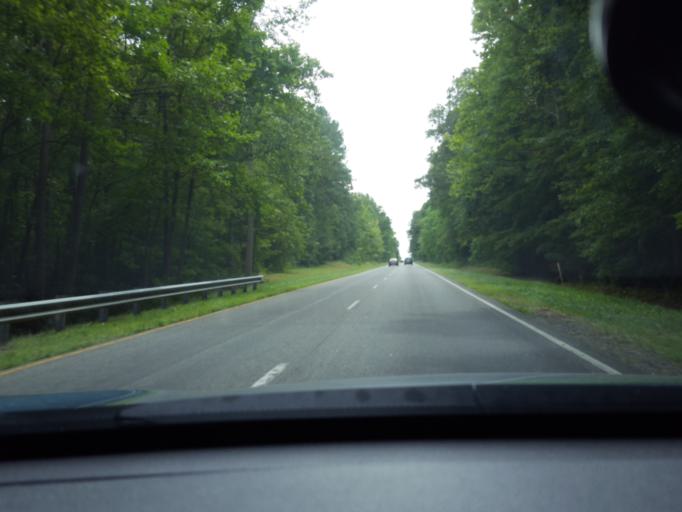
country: US
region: Virginia
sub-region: Caroline County
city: Bowling Green
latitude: 38.1321
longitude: -77.2379
